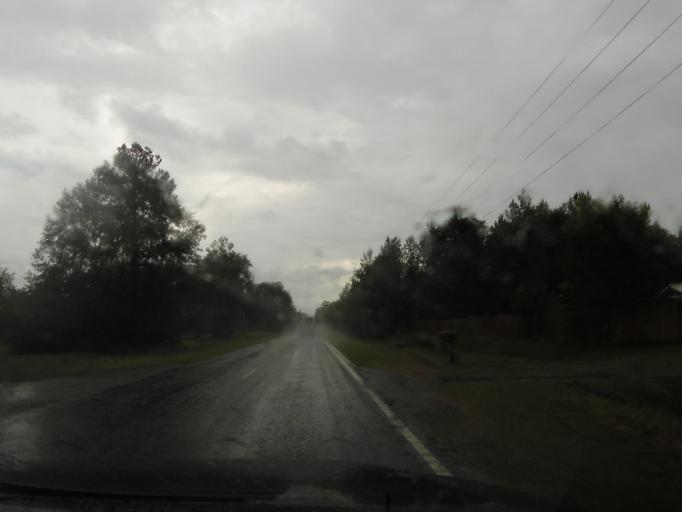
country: US
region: Florida
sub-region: Nassau County
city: Hilliard
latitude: 30.5320
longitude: -82.0389
